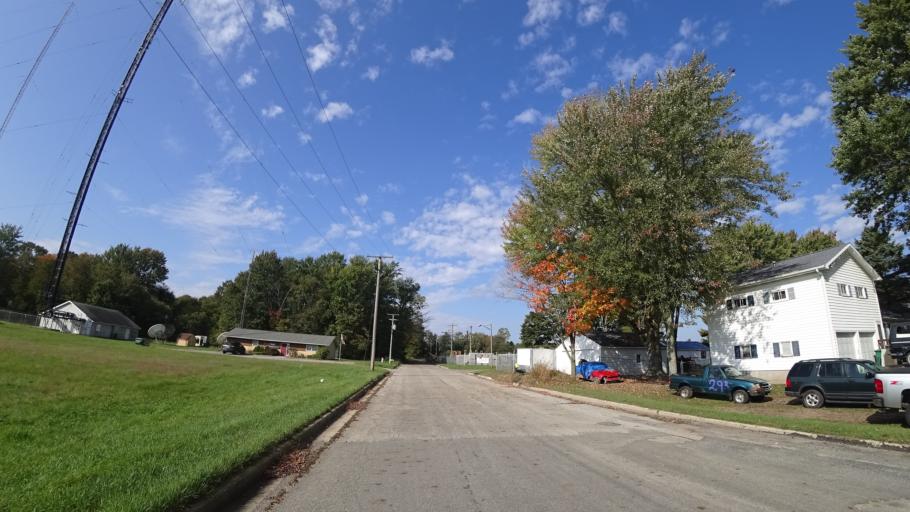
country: US
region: Michigan
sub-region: Saint Joseph County
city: Three Rivers
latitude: 41.9291
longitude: -85.6369
